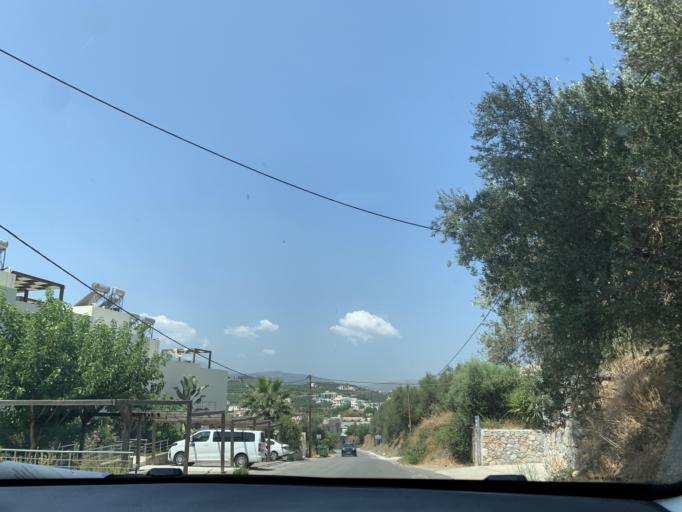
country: GR
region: Crete
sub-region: Nomos Chanias
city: Kalivai
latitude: 35.4490
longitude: 24.2053
